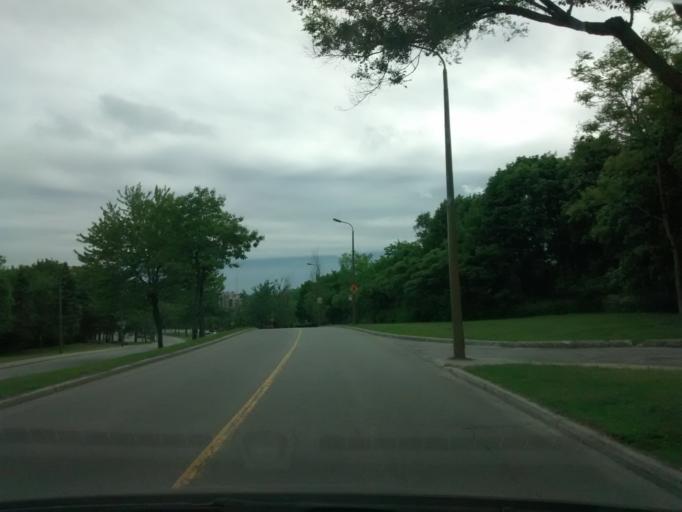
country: CA
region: Quebec
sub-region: Montreal
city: Montreal
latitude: 45.5019
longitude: -73.5974
